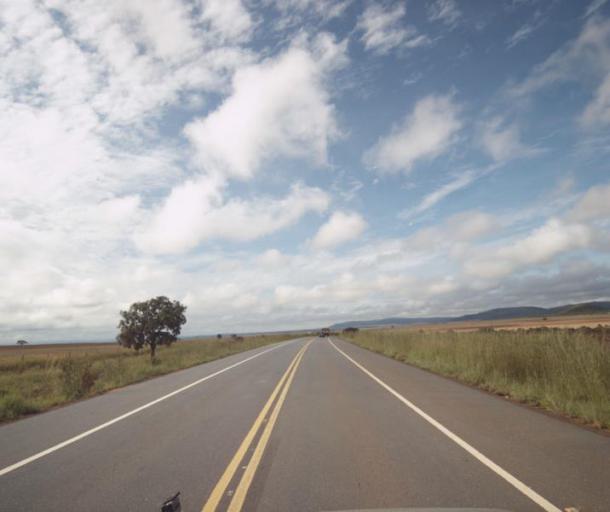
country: BR
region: Goias
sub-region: Barro Alto
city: Barro Alto
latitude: -15.2518
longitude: -48.6884
